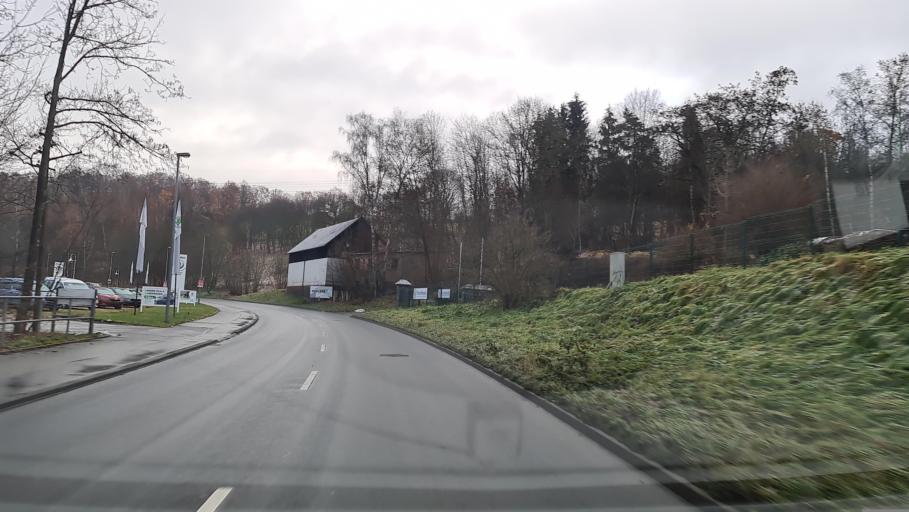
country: DE
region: Saxony
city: Mylau
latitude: 50.6170
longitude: 12.2788
